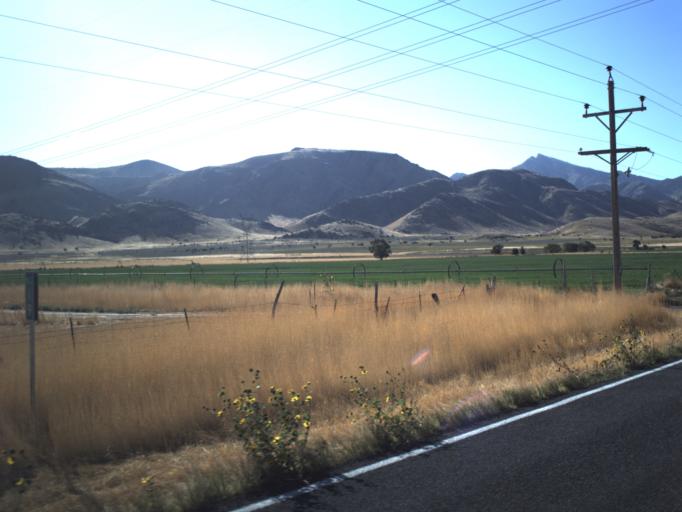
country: US
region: Utah
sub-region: Millard County
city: Delta
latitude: 39.4955
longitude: -112.2690
